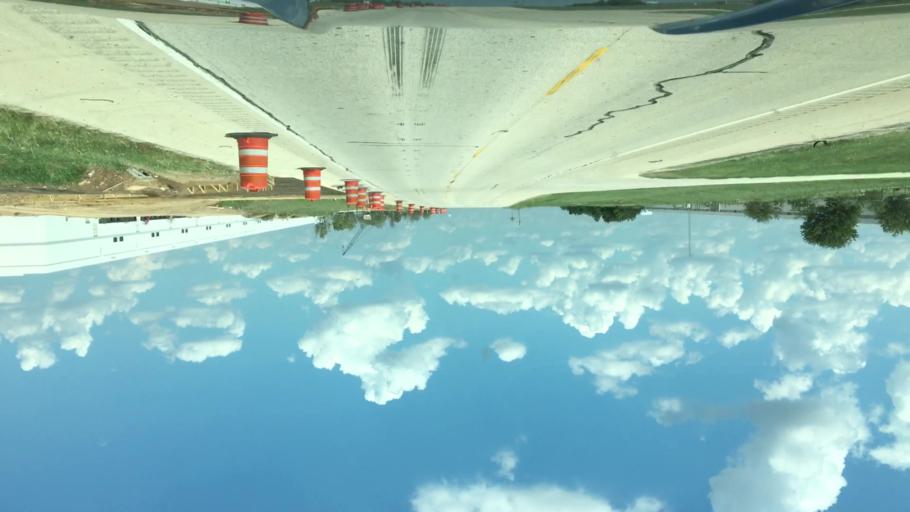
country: US
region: Texas
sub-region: Tarrant County
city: Haslet
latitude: 32.9835
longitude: -97.3419
